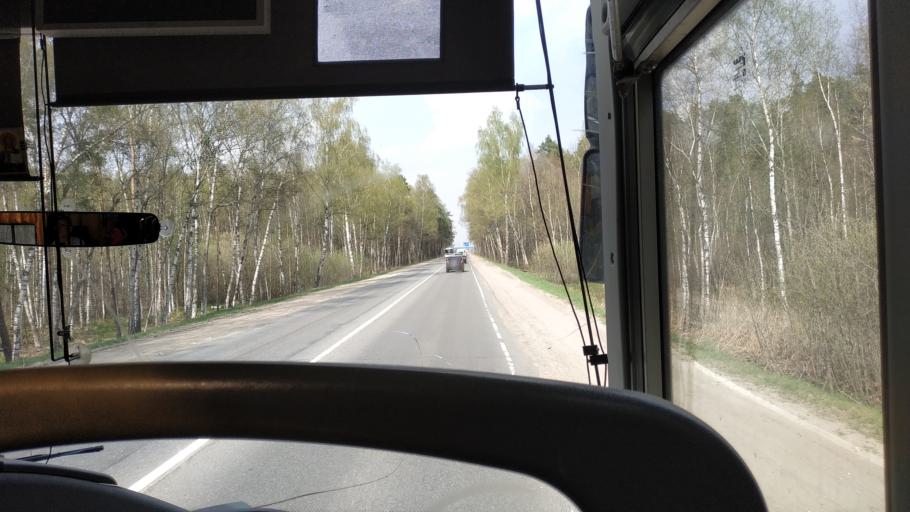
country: RU
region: Moskovskaya
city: Lytkarino
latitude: 55.6067
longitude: 37.9173
